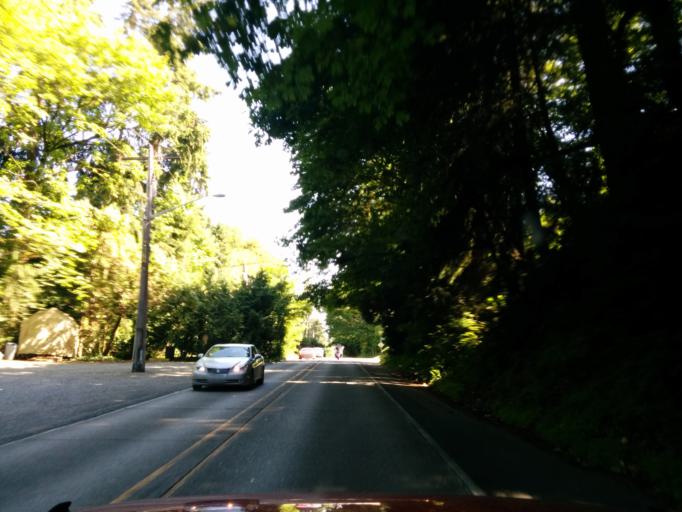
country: US
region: Washington
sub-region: King County
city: West Lake Sammamish
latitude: 47.6024
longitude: -122.1120
